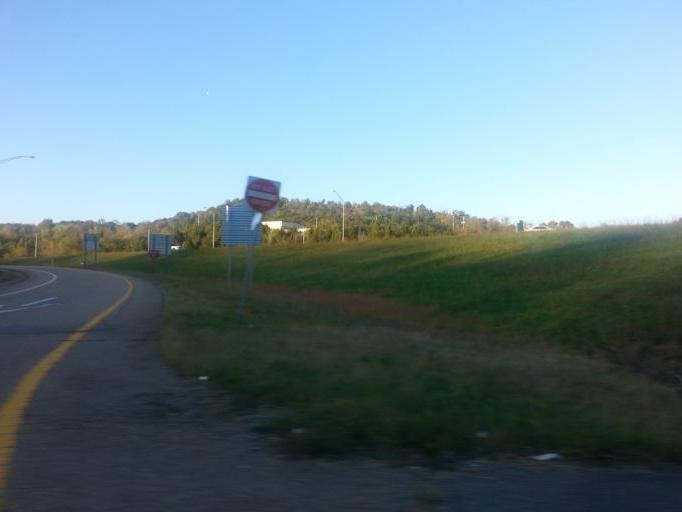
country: US
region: Tennessee
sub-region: Anderson County
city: Rocky Top
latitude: 36.2277
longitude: -84.1528
